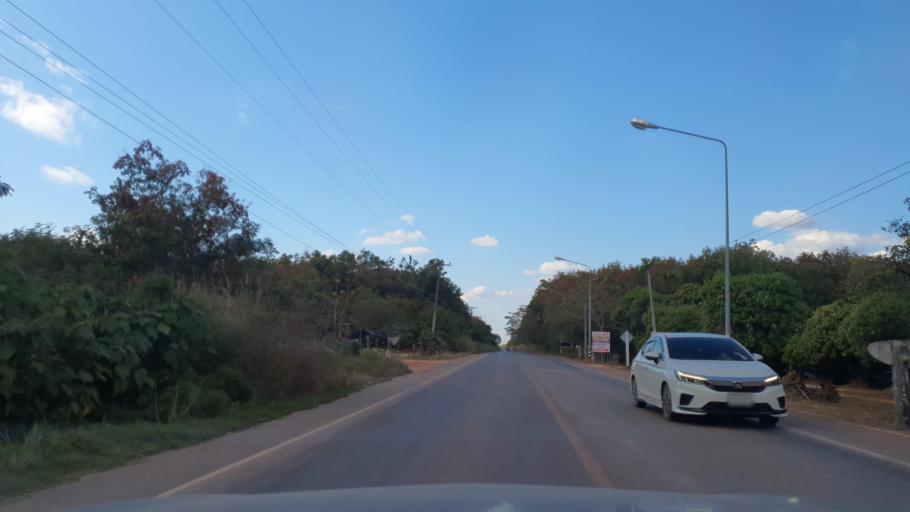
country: TH
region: Nong Khai
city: Bueng Khong Long
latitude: 17.9877
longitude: 104.0239
